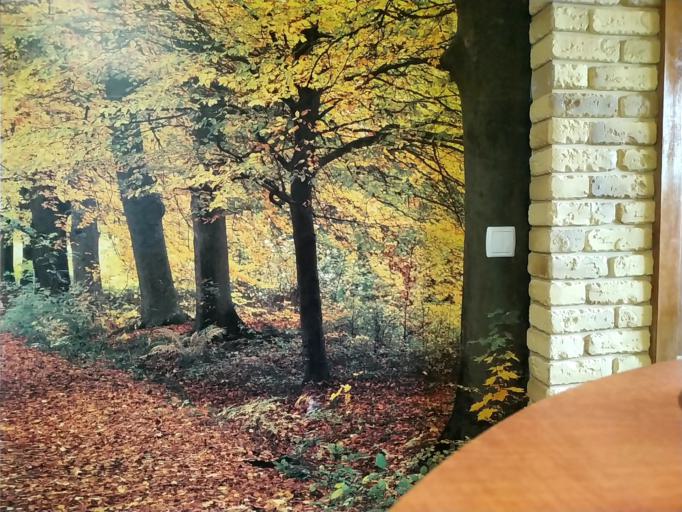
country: RU
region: Novgorod
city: Opechenskiy Posad
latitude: 58.2667
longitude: 34.0287
